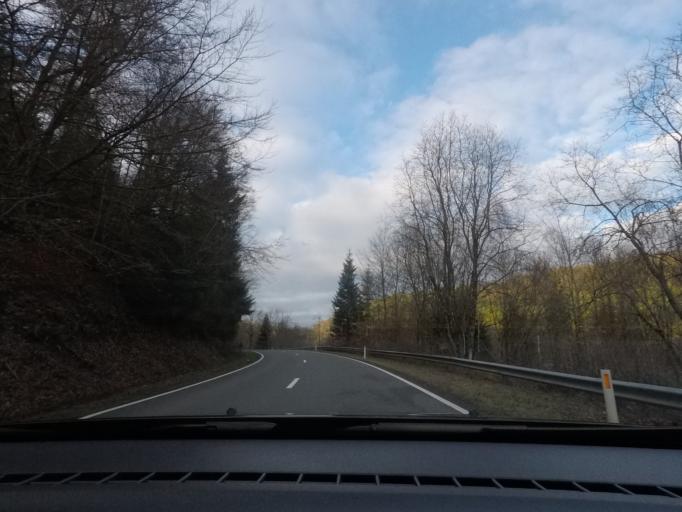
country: BE
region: Wallonia
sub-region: Province du Luxembourg
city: Leglise
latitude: 49.7482
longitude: 5.5267
